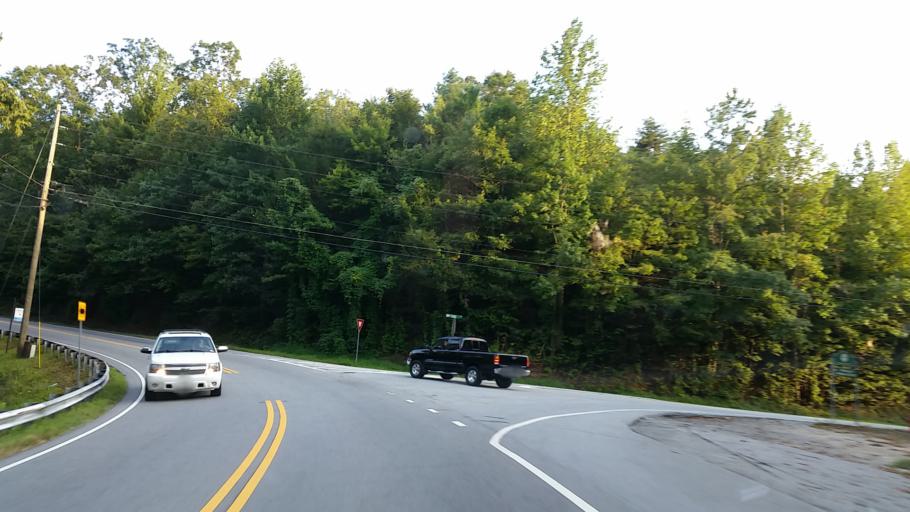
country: US
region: Georgia
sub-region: Lumpkin County
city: Dahlonega
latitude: 34.5508
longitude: -83.9958
